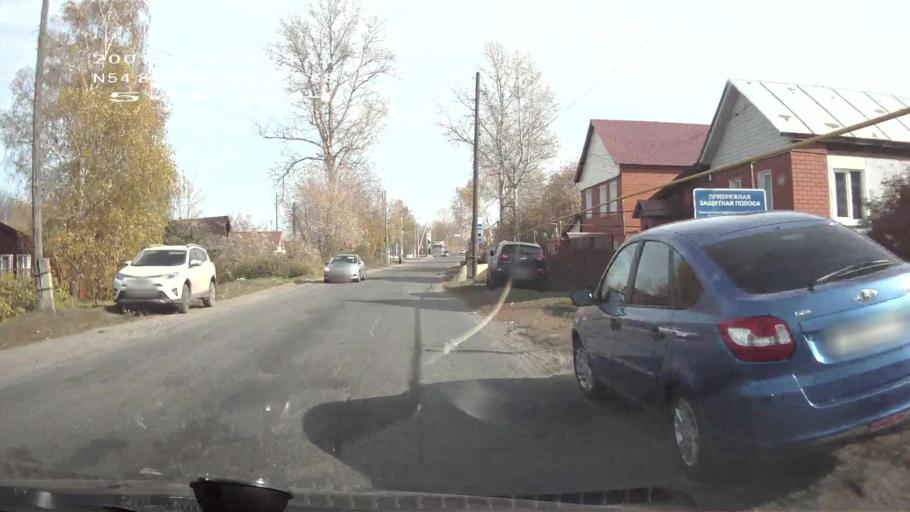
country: RU
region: Chuvashia
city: Alatyr'
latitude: 54.8475
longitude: 46.4976
